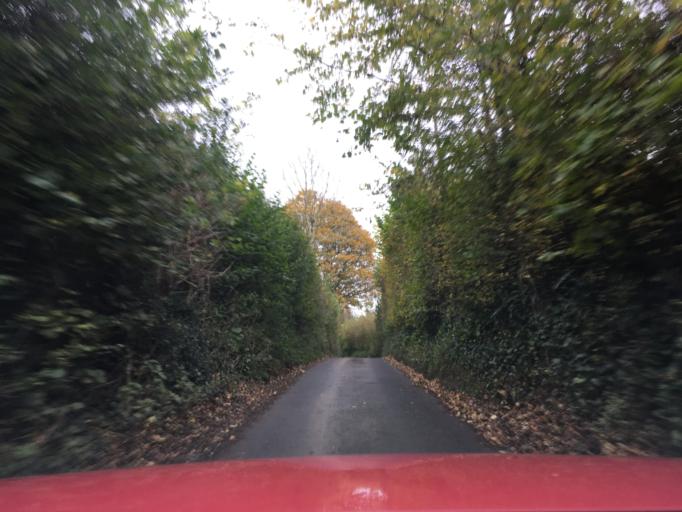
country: GB
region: England
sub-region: Somerset
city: Ilminster
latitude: 50.9550
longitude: -2.8797
